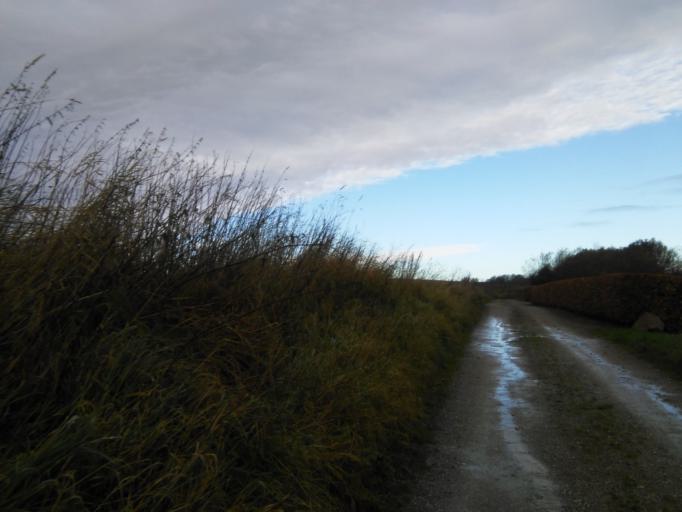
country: DK
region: Central Jutland
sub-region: Arhus Kommune
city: Marslet
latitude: 56.0884
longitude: 10.1778
